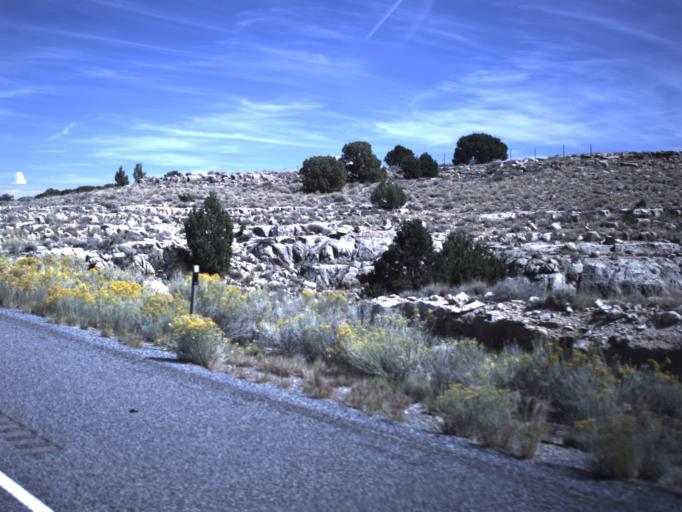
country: US
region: Utah
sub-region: Emery County
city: Castle Dale
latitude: 38.9044
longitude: -110.5562
